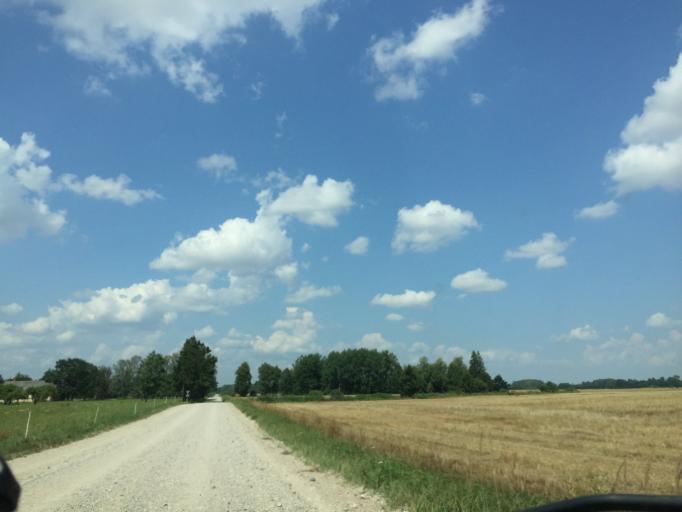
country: LT
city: Zagare
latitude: 56.3770
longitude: 23.2793
